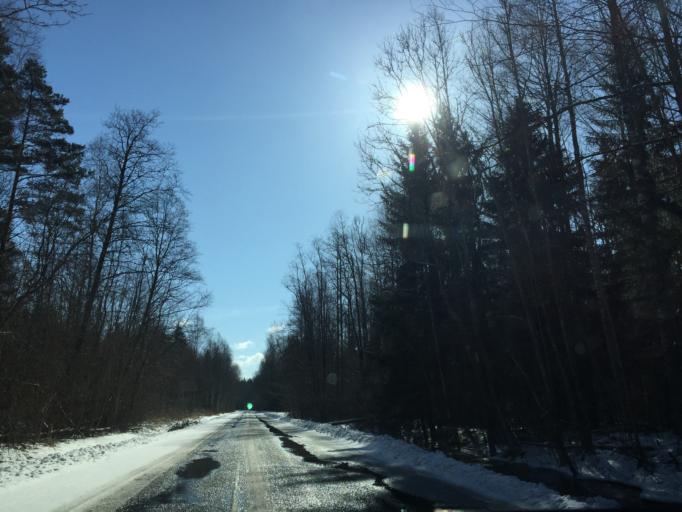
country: LV
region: Salacgrivas
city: Ainazi
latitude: 57.9991
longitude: 24.5298
